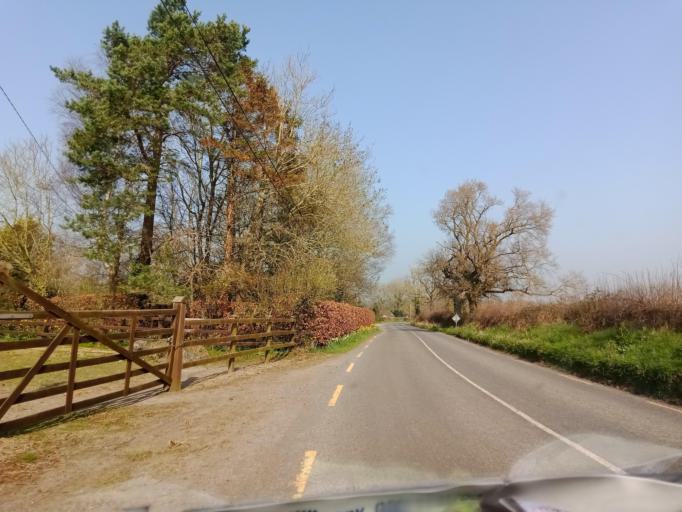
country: IE
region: Leinster
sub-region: Kilkenny
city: Callan
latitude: 52.5122
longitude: -7.3850
